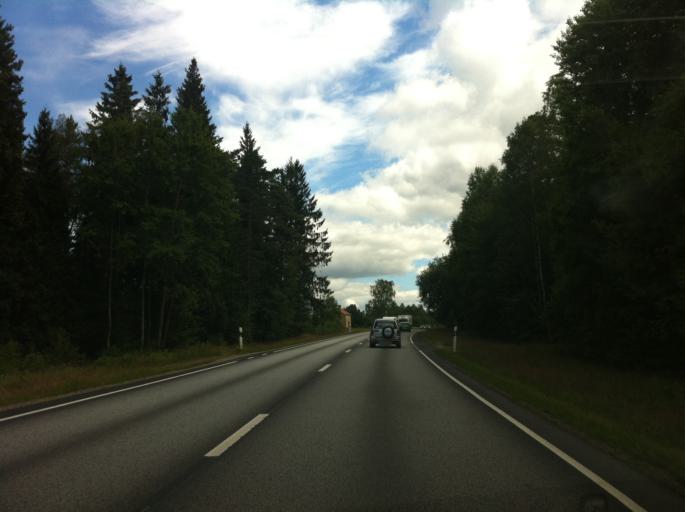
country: SE
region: Joenkoeping
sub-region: Gislaveds Kommun
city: Smalandsstenar
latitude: 57.1782
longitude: 13.4238
